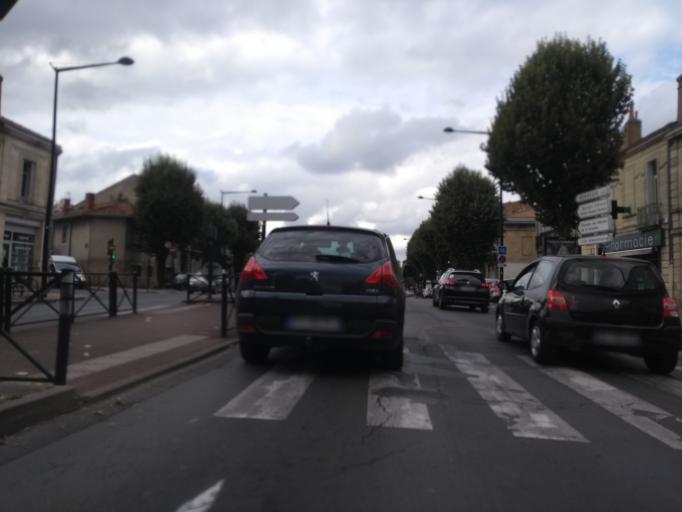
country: FR
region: Aquitaine
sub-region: Departement de la Gironde
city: Bordeaux
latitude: 44.8274
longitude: -0.5923
